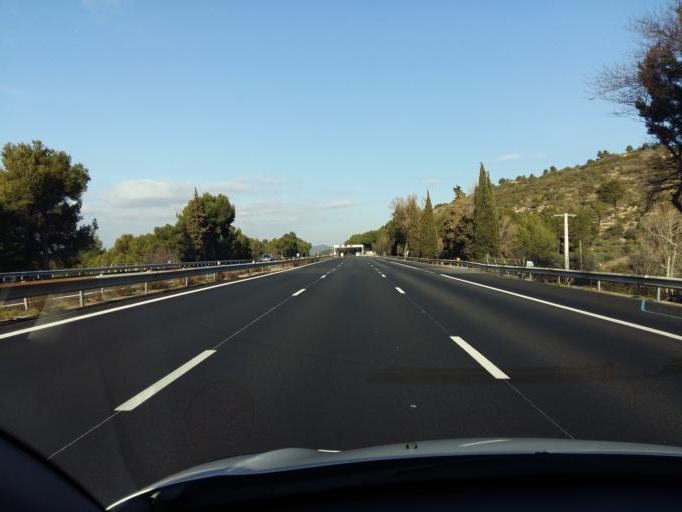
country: FR
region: Provence-Alpes-Cote d'Azur
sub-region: Departement des Bouches-du-Rhone
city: Salon-de-Provence
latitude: 43.6473
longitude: 5.1115
